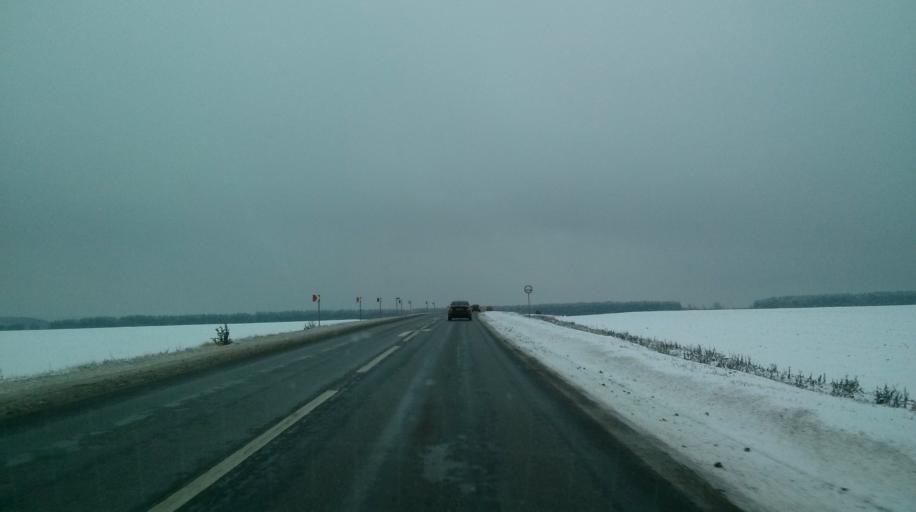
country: RU
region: Nizjnij Novgorod
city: Bogorodsk
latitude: 56.0919
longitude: 43.5746
